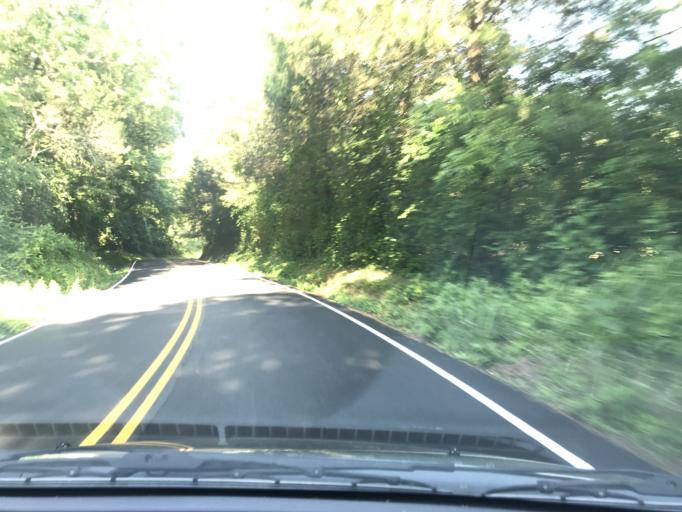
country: US
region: Tennessee
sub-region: Loudon County
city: Loudon
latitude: 35.7922
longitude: -84.3606
